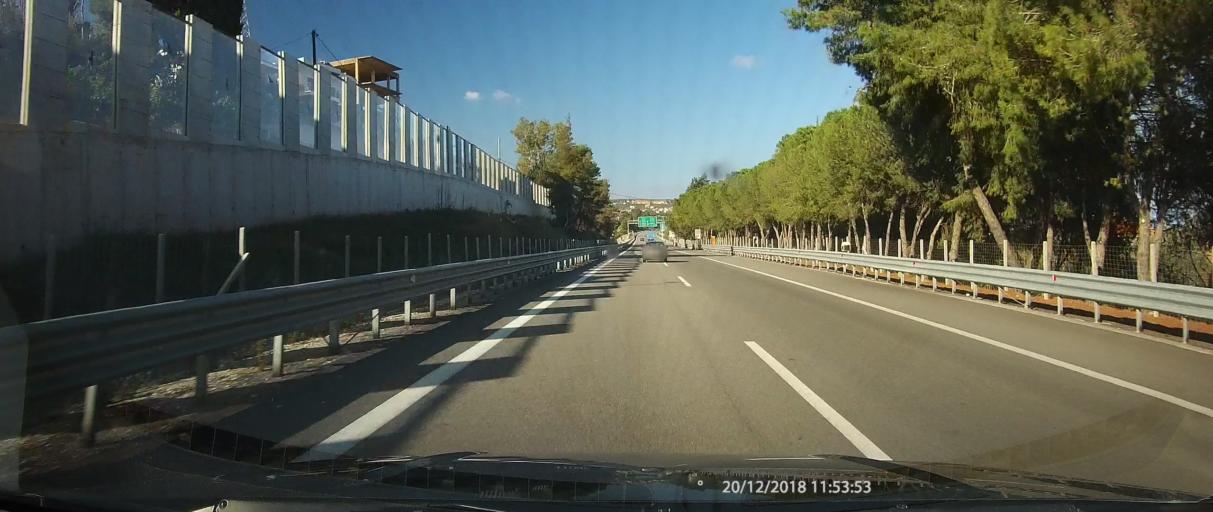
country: GR
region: West Greece
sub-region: Nomos Achaias
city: Aiyira
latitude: 38.1478
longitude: 22.3534
